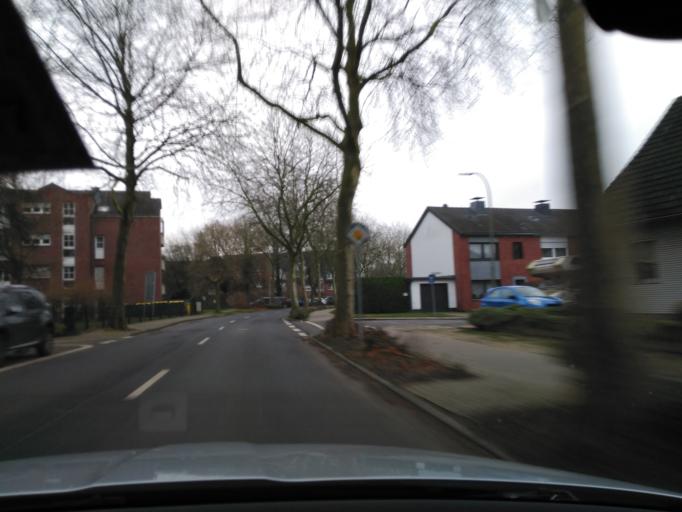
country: DE
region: North Rhine-Westphalia
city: Wegberg
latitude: 51.1373
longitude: 6.2948
